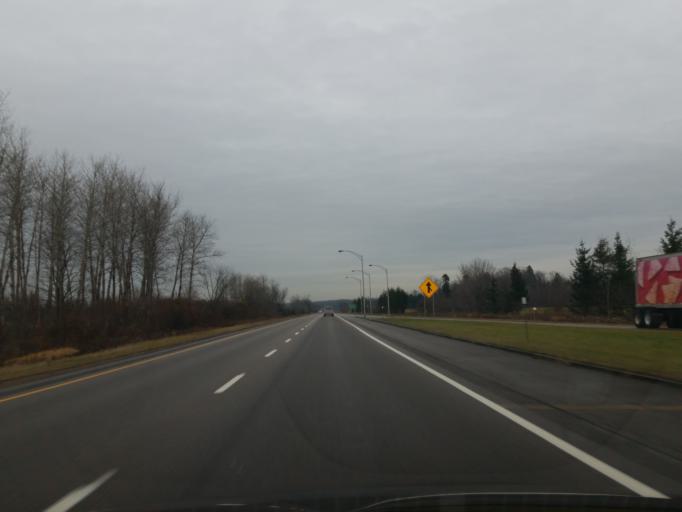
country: CA
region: Quebec
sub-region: Capitale-Nationale
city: Saint-Augustin-de-Desmaures
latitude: 46.7472
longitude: -71.5186
